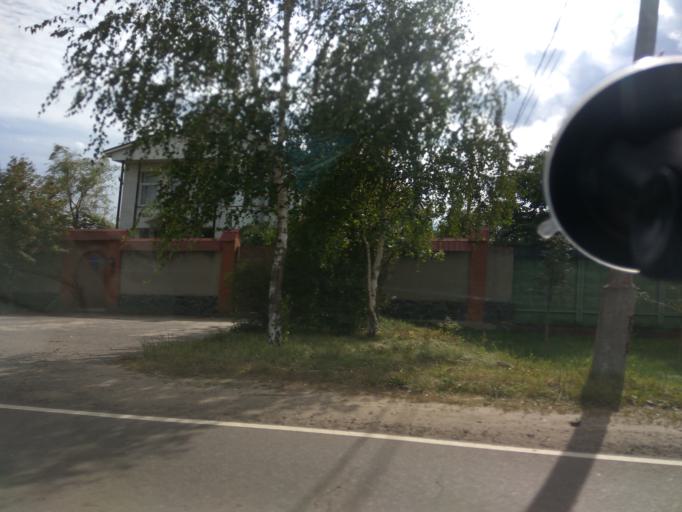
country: RU
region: Moskovskaya
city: Ramenskoye
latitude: 55.5774
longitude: 38.2817
